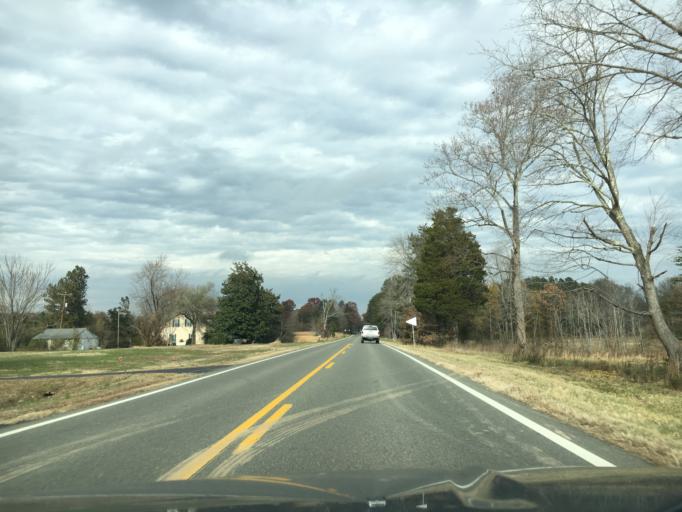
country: US
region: Virginia
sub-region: Prince Edward County
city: Farmville
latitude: 37.4109
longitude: -78.3556
